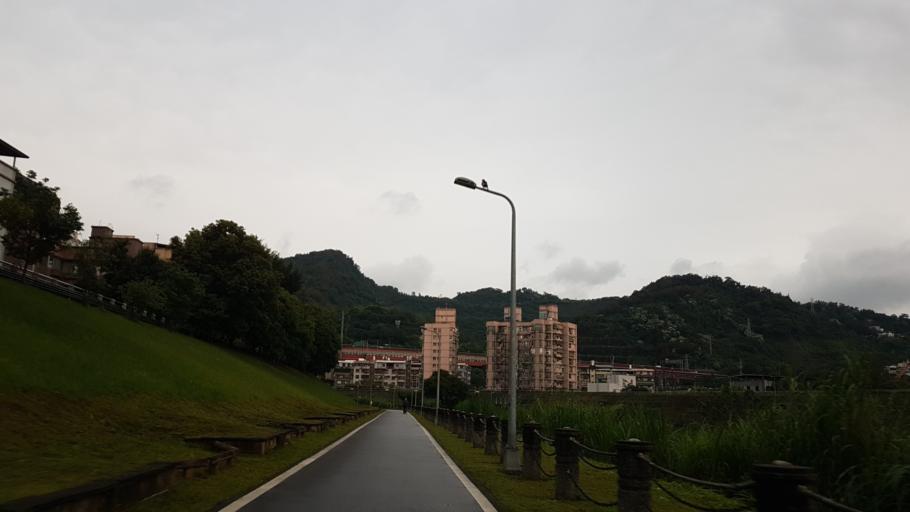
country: TW
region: Taipei
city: Taipei
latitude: 24.9786
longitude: 121.5540
